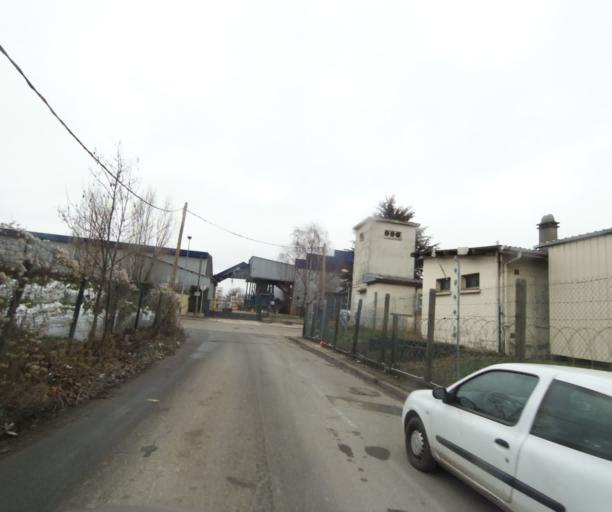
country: FR
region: Ile-de-France
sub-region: Departement du Val-de-Marne
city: Ablon-sur-Seine
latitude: 48.7377
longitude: 2.4306
